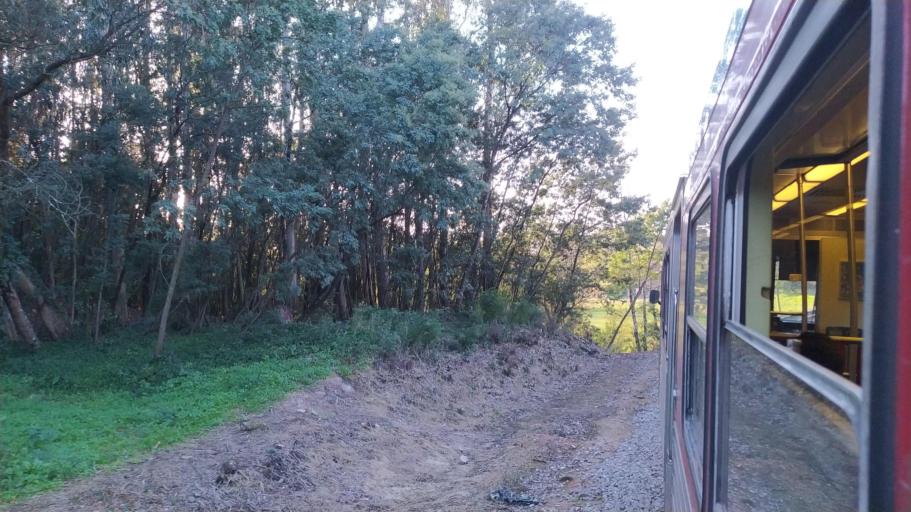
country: PT
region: Aveiro
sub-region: Aveiro
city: Eixo
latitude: 40.6012
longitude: -8.5247
